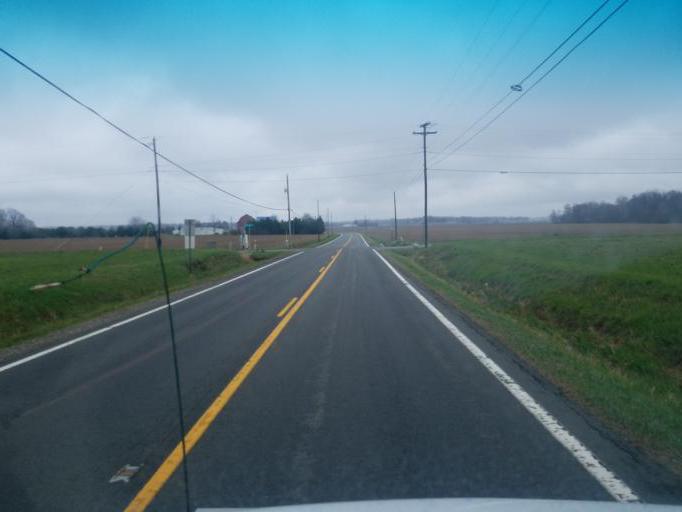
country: US
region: Ohio
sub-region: Huron County
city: Plymouth
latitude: 40.9453
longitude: -82.6671
